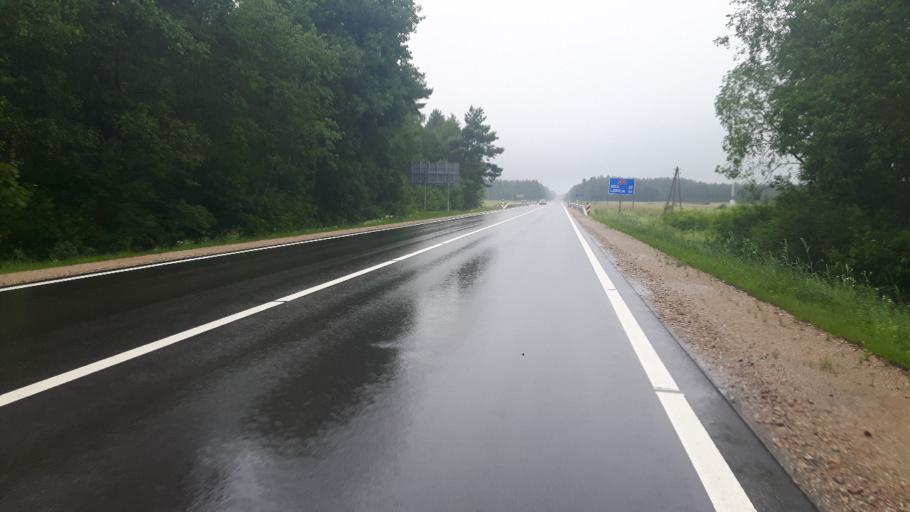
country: LV
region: Rucavas
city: Rucava
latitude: 56.1598
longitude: 21.1468
